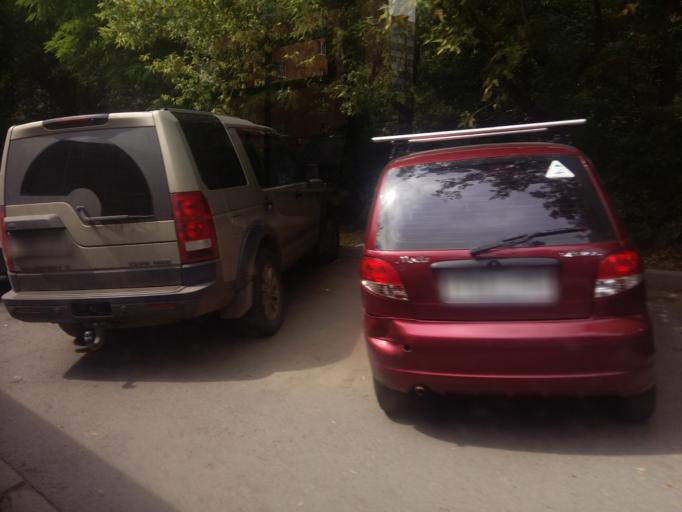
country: RU
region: Rostov
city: Imeni Chkalova
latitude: 47.2886
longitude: 39.7573
